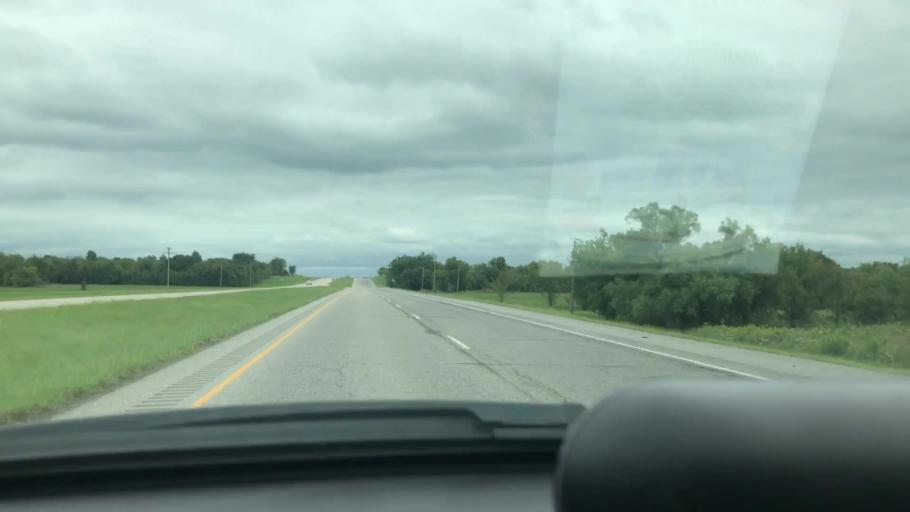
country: US
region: Oklahoma
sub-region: Wagoner County
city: Wagoner
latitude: 35.9859
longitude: -95.3760
